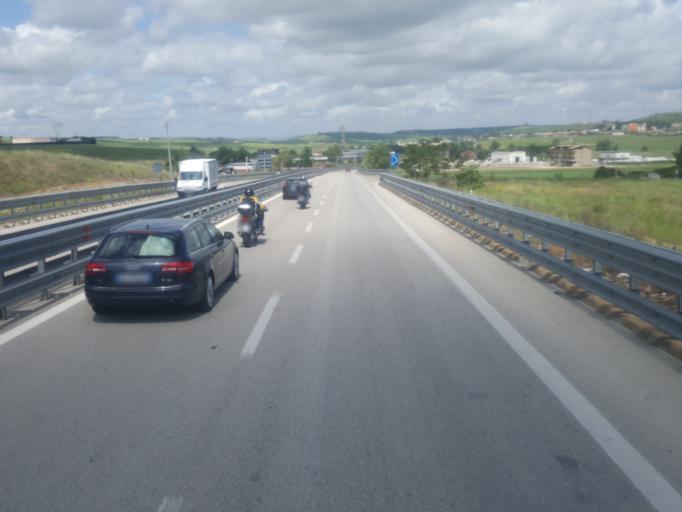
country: IT
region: Basilicate
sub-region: Provincia di Matera
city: Matera
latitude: 40.7055
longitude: 16.5841
